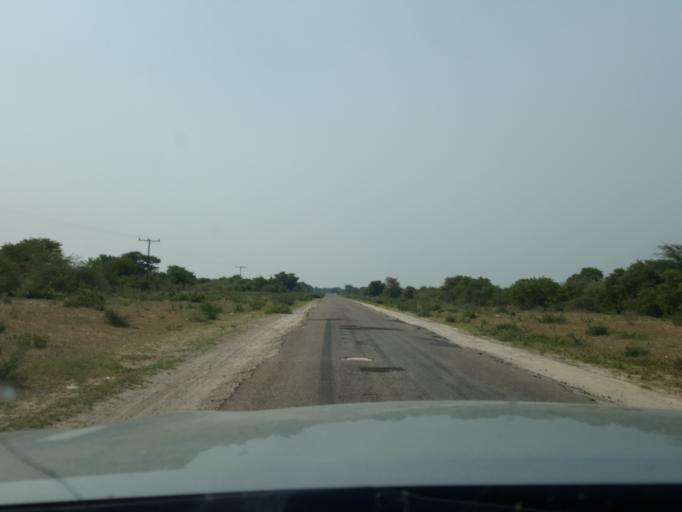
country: BW
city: Nokaneng
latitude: -19.1045
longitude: 22.2709
